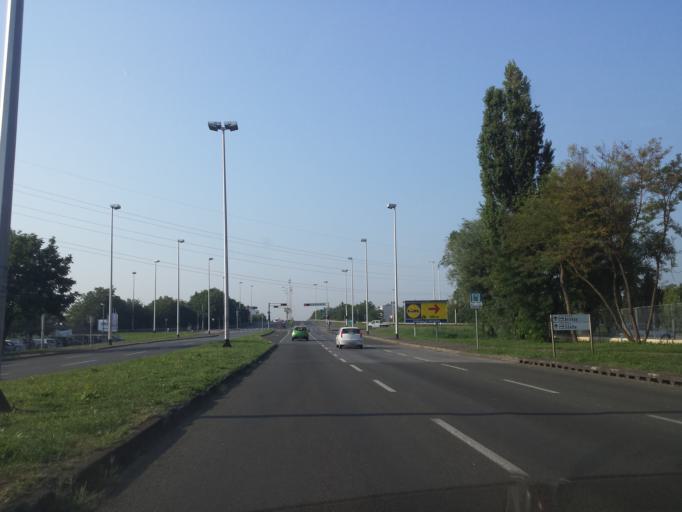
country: HR
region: Grad Zagreb
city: Novi Zagreb
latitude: 45.7612
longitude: 15.9903
